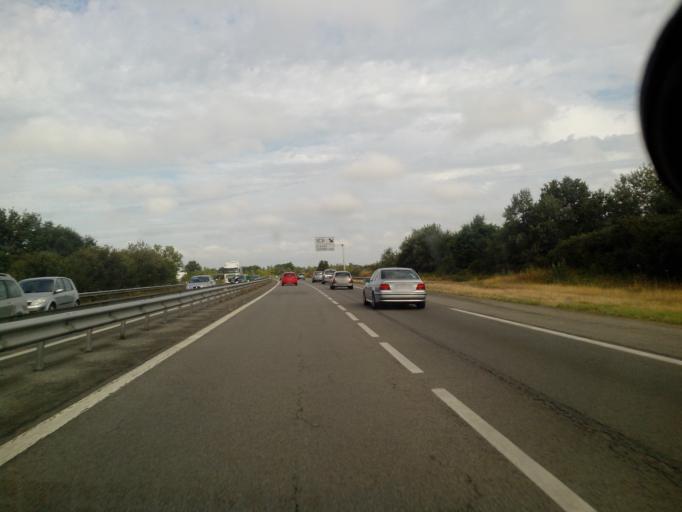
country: FR
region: Pays de la Loire
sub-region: Departement de la Loire-Atlantique
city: Savenay
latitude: 47.3738
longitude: -1.9328
